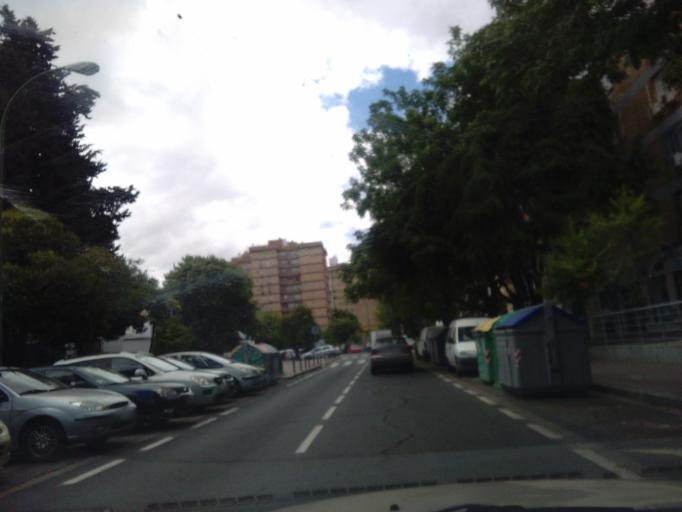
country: ES
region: Andalusia
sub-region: Provincia de Sevilla
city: Sevilla
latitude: 37.3752
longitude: -5.9529
